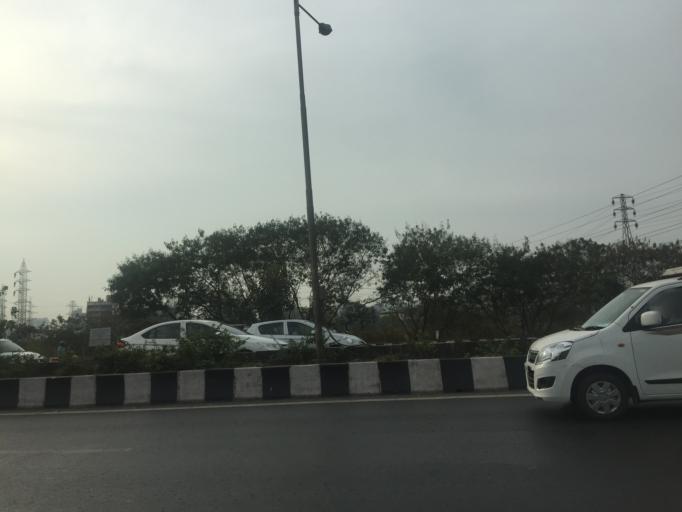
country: IN
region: Maharashtra
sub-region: Thane
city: Airoli
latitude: 19.1467
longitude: 72.9519
